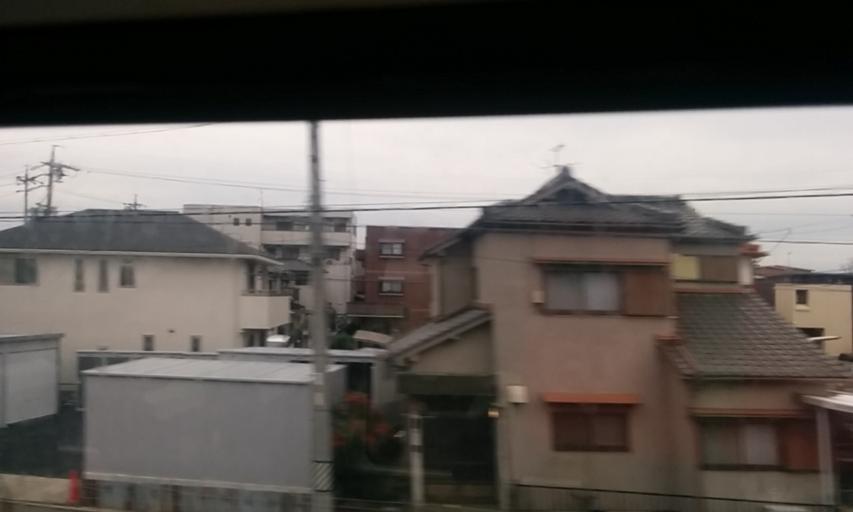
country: JP
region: Aichi
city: Kasugai
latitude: 35.2106
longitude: 136.9526
